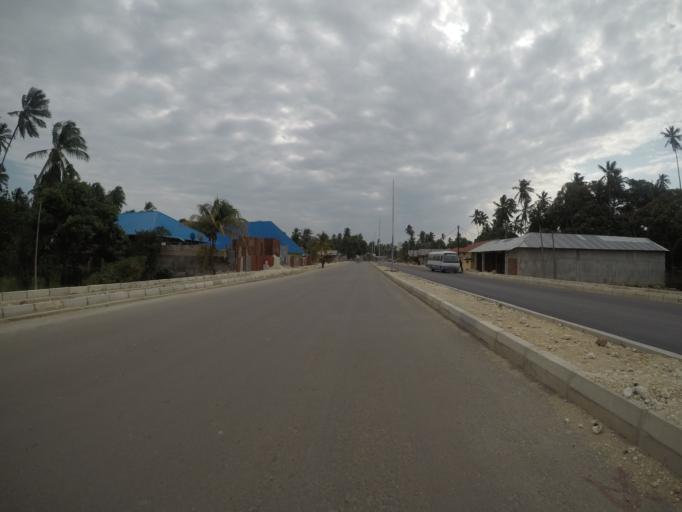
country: TZ
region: Zanzibar Central/South
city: Koani
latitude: -6.1960
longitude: 39.2747
